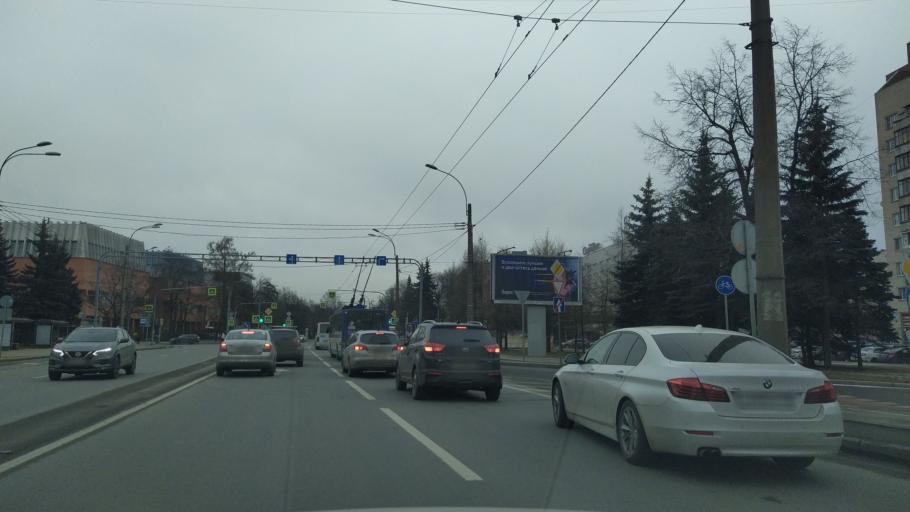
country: RU
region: St.-Petersburg
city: Sosnovka
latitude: 60.0071
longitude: 30.3535
